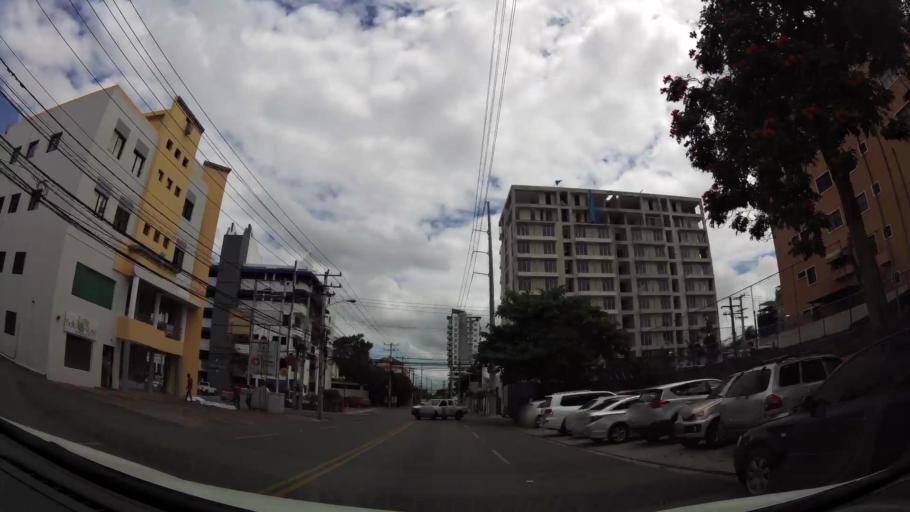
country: DO
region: Nacional
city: La Julia
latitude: 18.4801
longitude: -69.9410
